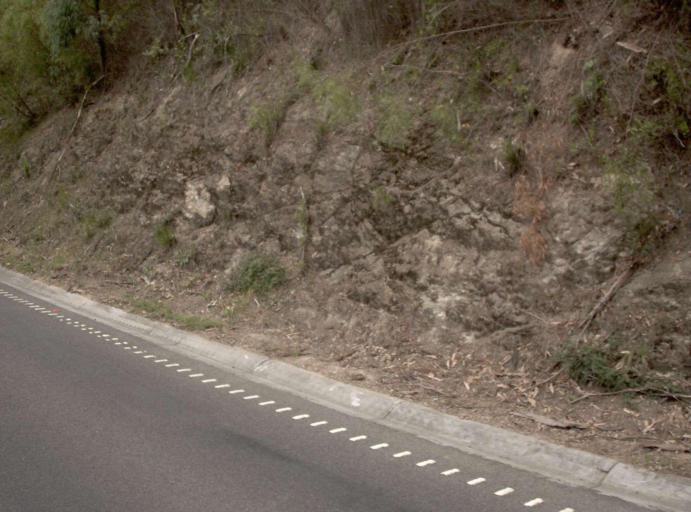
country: AU
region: Victoria
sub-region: Yarra Ranges
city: Yarra Glen
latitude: -37.5458
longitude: 145.4164
